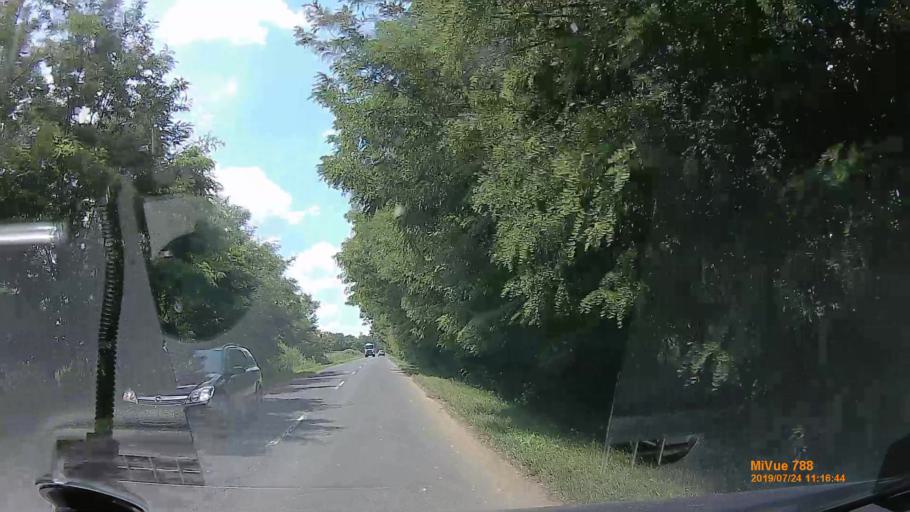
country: HU
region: Szabolcs-Szatmar-Bereg
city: Tarpa
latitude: 48.1775
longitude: 22.4634
